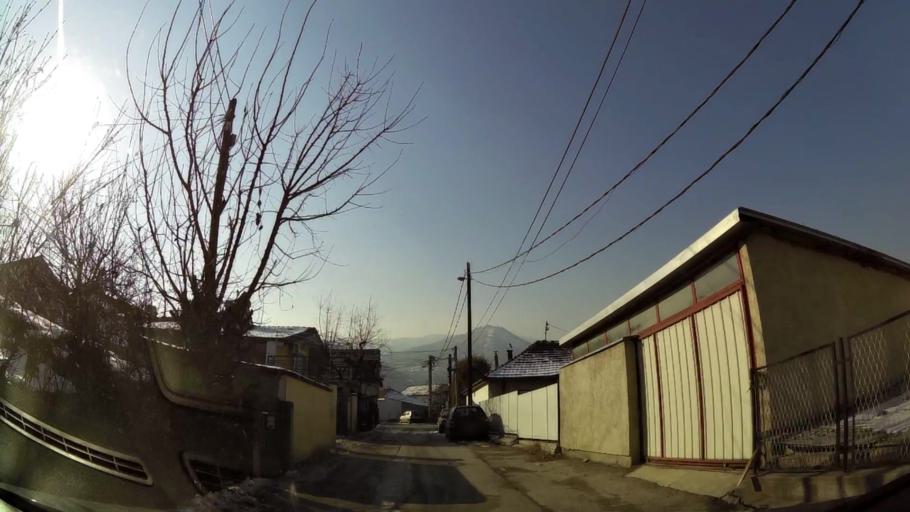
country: MK
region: Kisela Voda
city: Usje
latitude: 41.9709
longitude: 21.4497
